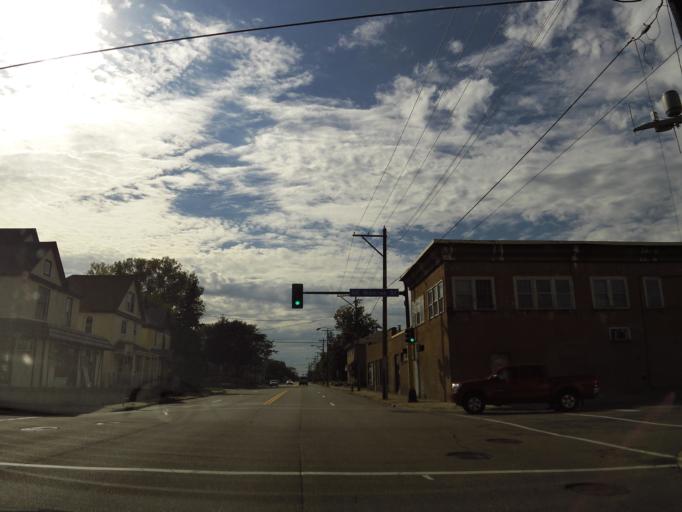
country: US
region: Minnesota
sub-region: Anoka County
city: Columbia Heights
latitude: 45.0132
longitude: -93.2523
